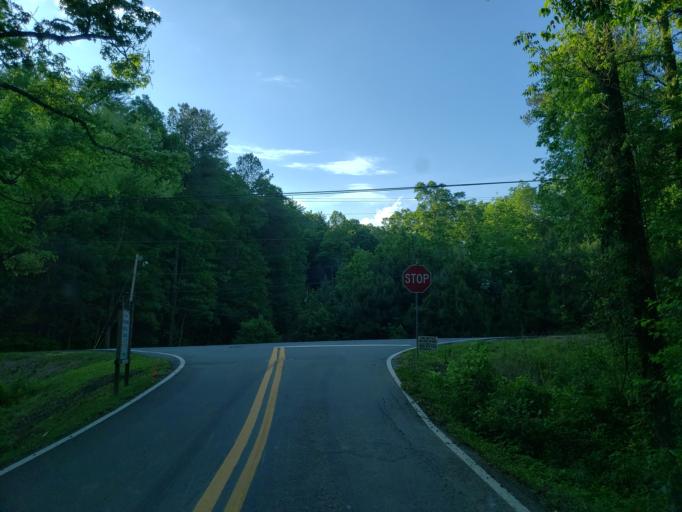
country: US
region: Georgia
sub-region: Murray County
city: Chatsworth
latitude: 34.6653
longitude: -84.6473
